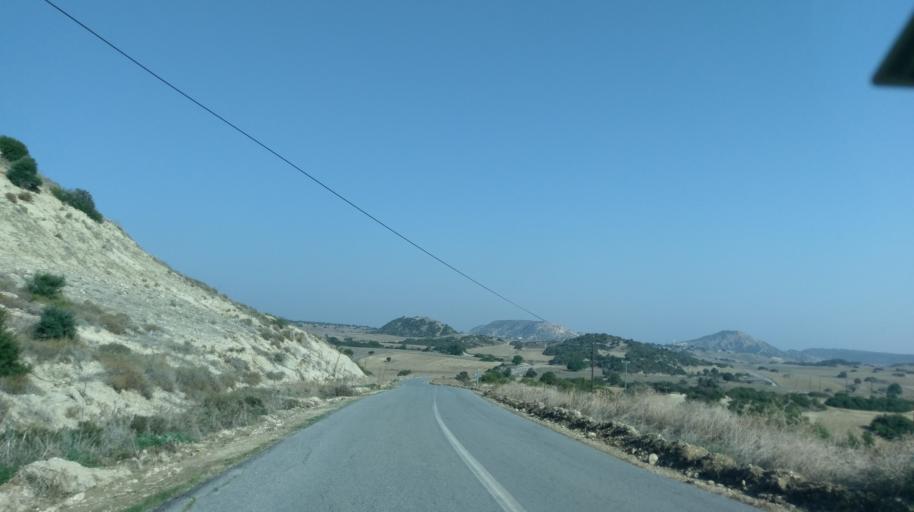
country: CY
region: Ammochostos
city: Leonarisso
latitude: 35.5059
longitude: 34.2511
